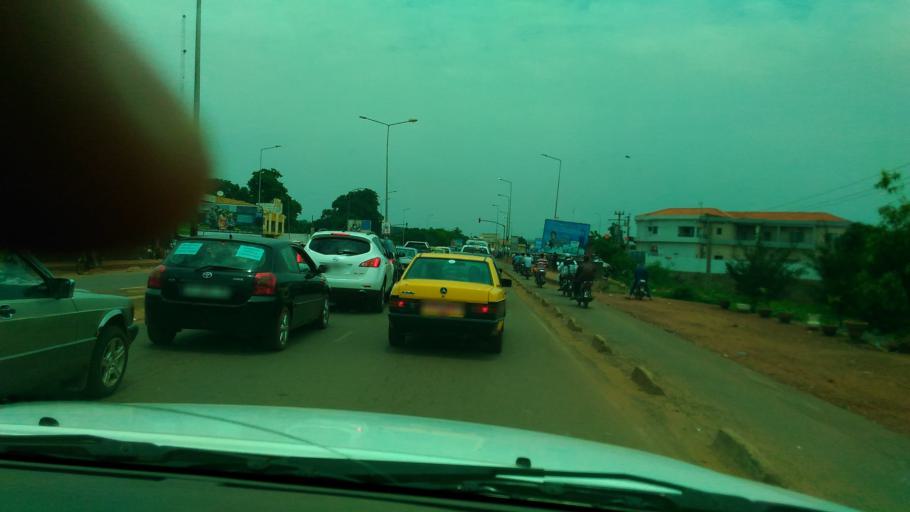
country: ML
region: Bamako
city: Bamako
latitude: 12.6081
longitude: -7.9744
